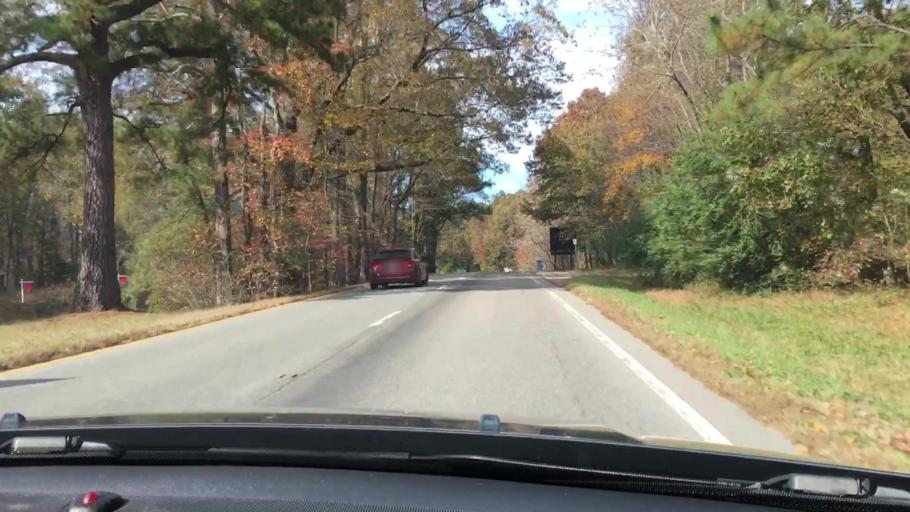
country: US
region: Virginia
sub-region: James City County
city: Williamsburg
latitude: 37.3322
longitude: -76.7448
